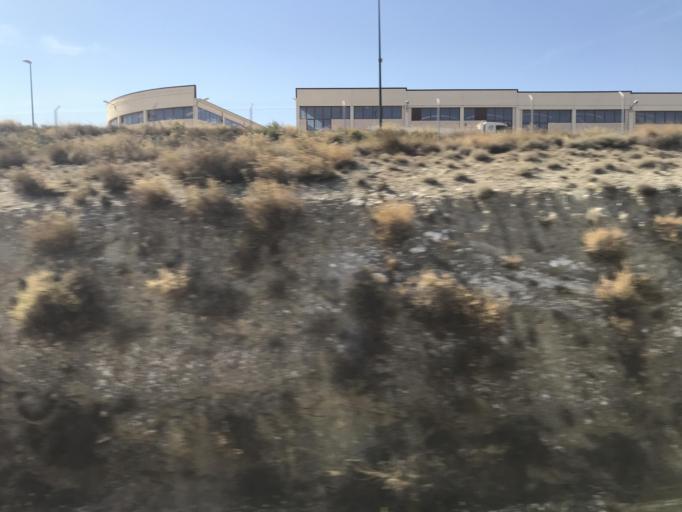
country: ES
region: Aragon
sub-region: Provincia de Zaragoza
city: El Burgo de Ebro
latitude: 41.5858
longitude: -0.8199
